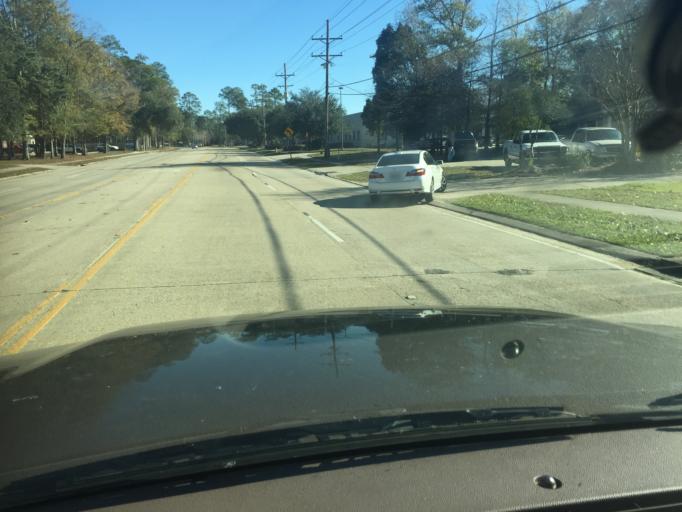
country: US
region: Louisiana
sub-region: Saint Tammany Parish
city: Slidell
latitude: 30.2997
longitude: -89.7565
